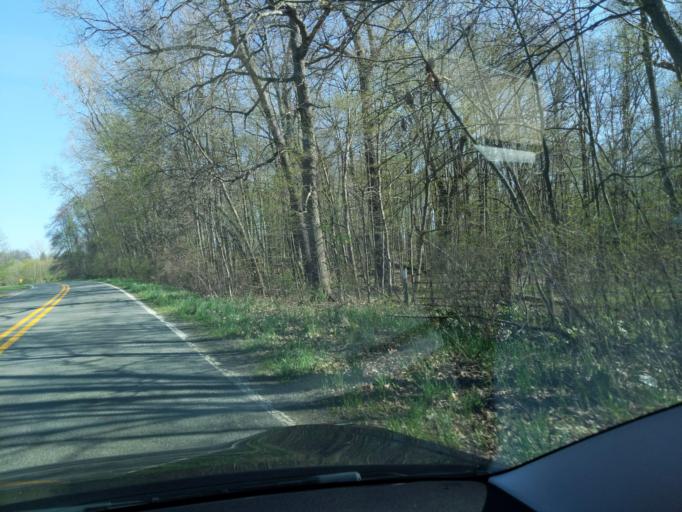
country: US
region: Michigan
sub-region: Ingham County
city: Stockbridge
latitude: 42.4444
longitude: -84.1008
